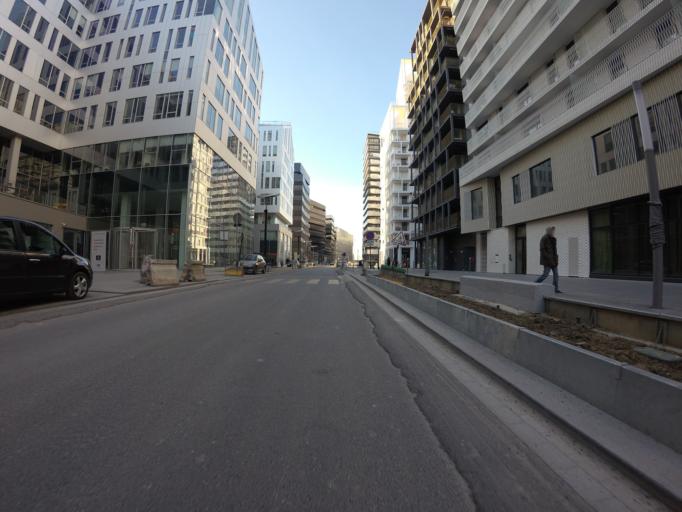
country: FR
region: Ile-de-France
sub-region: Departement des Hauts-de-Seine
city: Clichy
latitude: 48.8899
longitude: 2.3126
